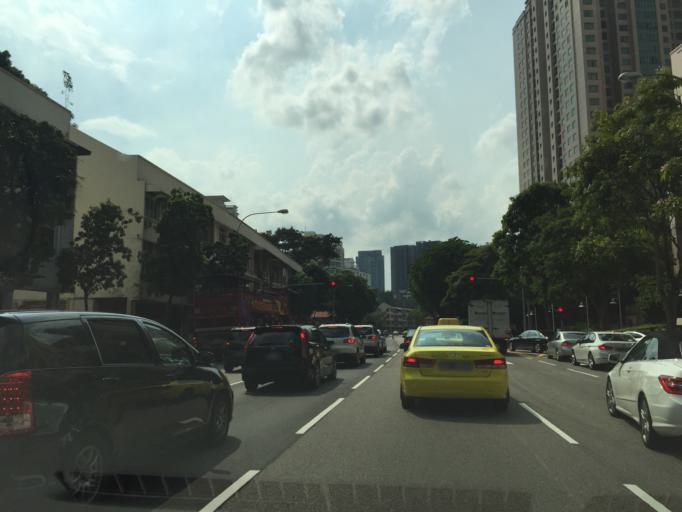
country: SG
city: Singapore
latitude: 1.2936
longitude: 103.8312
